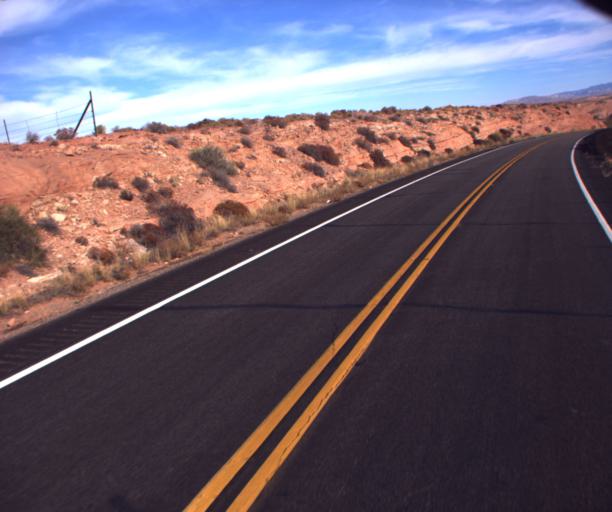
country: US
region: Arizona
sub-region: Navajo County
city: Kayenta
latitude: 36.9464
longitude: -109.7185
